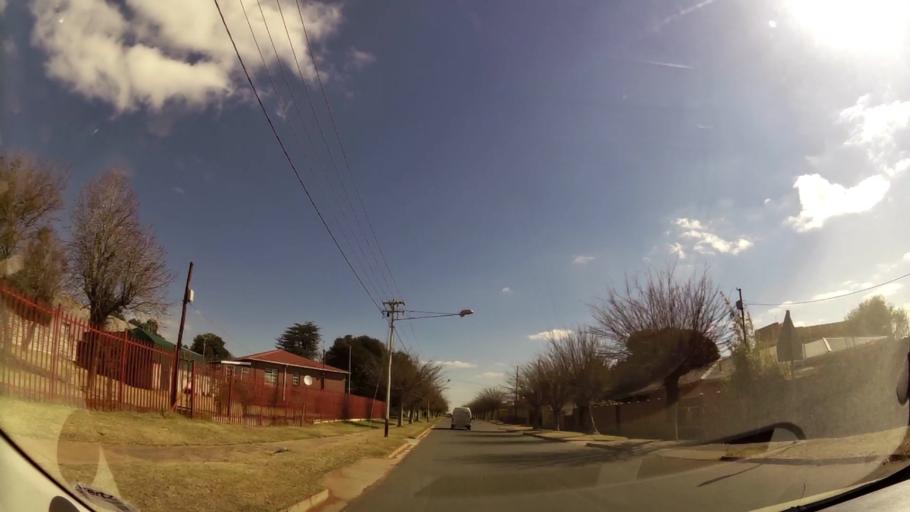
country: ZA
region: Gauteng
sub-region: West Rand District Municipality
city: Krugersdorp
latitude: -26.1090
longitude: 27.7841
